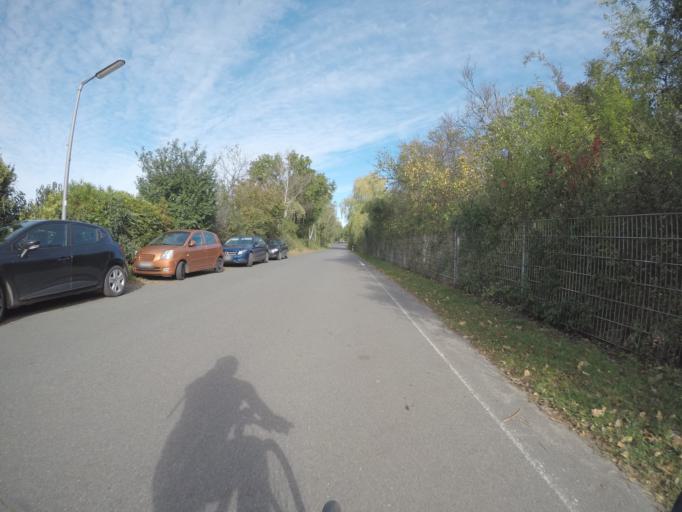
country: DE
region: Berlin
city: Marienfelde
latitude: 52.4019
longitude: 13.3616
